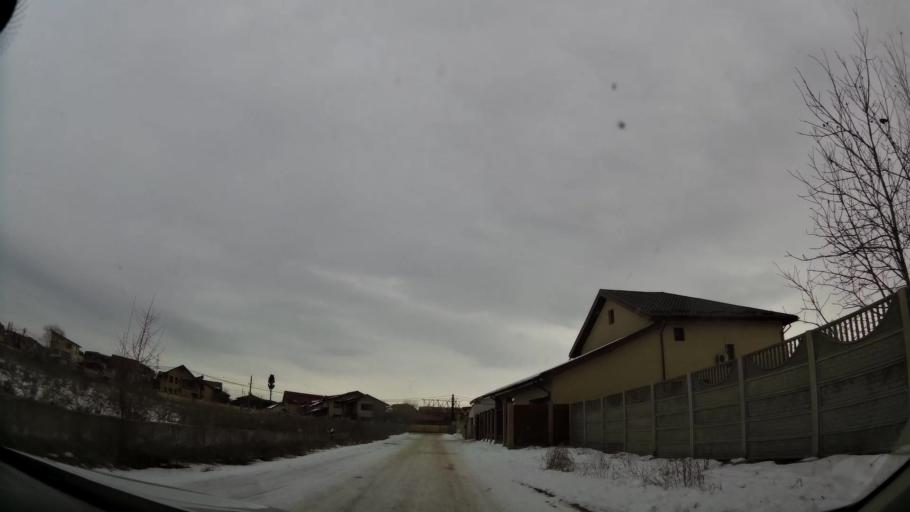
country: RO
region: Ilfov
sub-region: Comuna Pantelimon
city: Pantelimon
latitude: 44.4544
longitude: 26.2188
